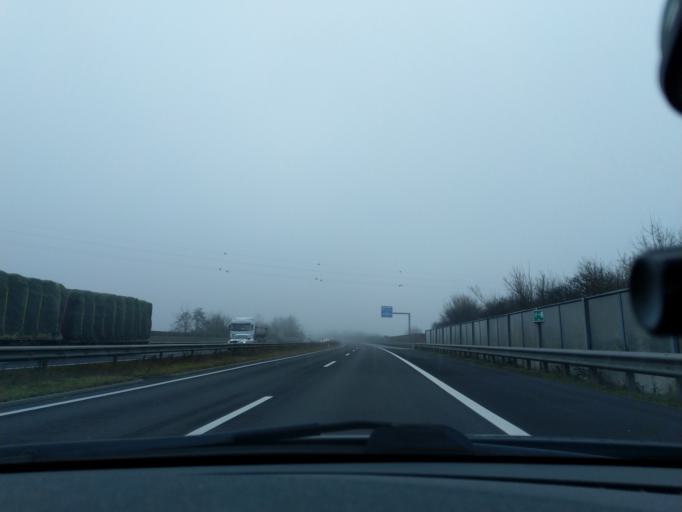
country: AT
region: Upper Austria
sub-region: Politischer Bezirk Urfahr-Umgebung
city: Engerwitzdorf
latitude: 48.3380
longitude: 14.4403
